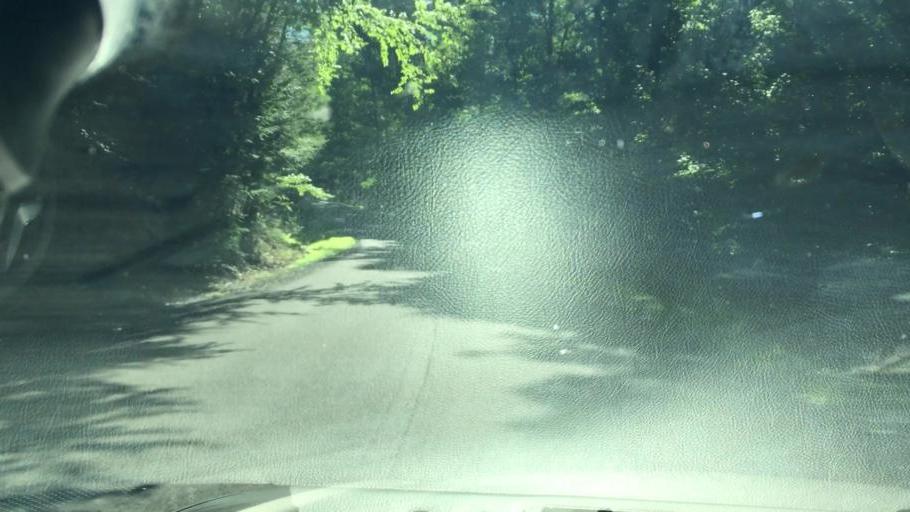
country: US
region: Pennsylvania
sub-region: Luzerne County
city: Freeland
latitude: 41.0364
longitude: -75.9399
